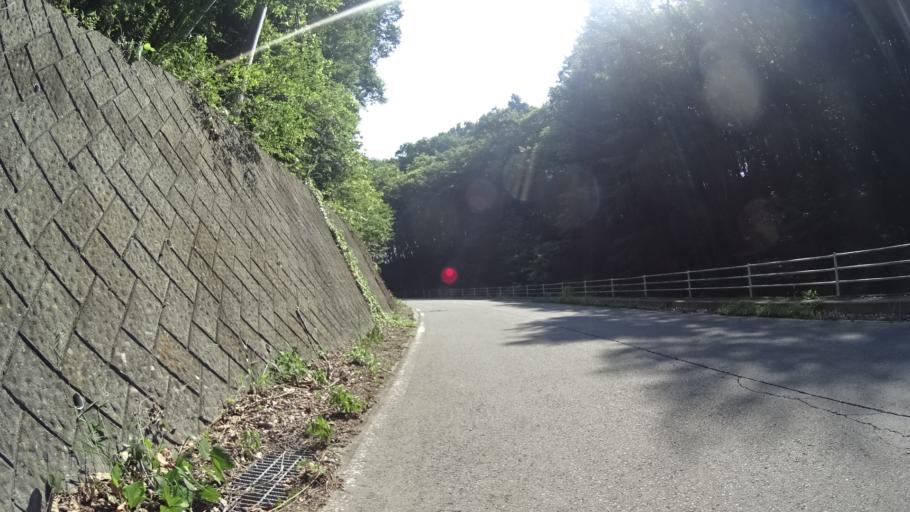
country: JP
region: Yamanashi
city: Nirasaki
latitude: 35.8650
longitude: 138.3265
